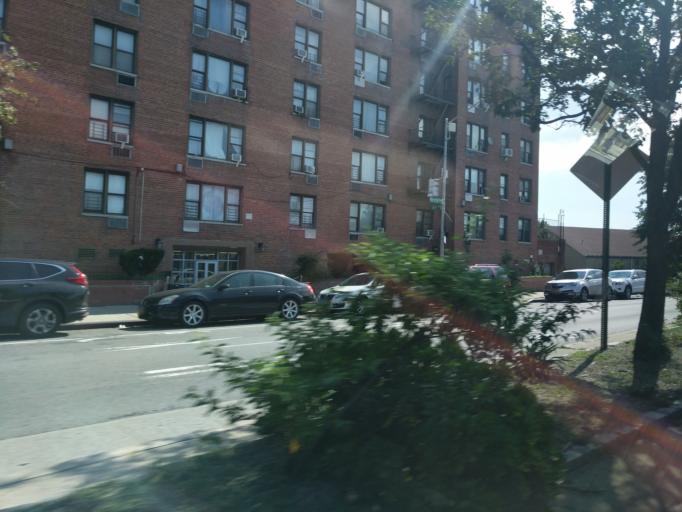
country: US
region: New York
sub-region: Queens County
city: Jamaica
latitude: 40.6967
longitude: -73.7837
